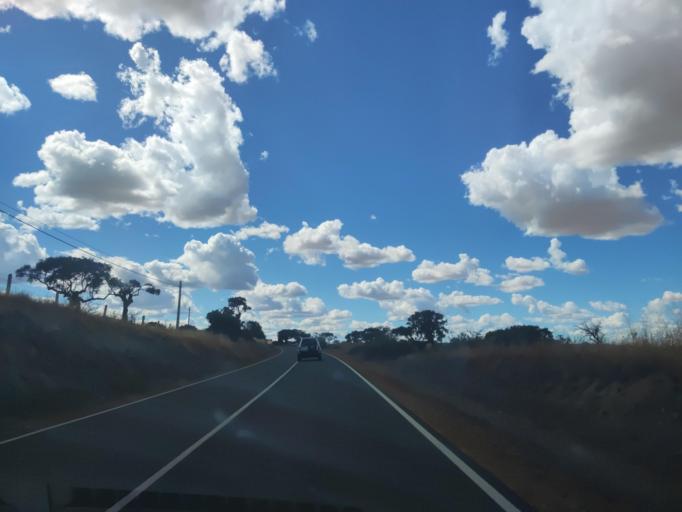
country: ES
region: Castille and Leon
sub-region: Provincia de Salamanca
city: Tamames
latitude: 40.6514
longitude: -6.0821
